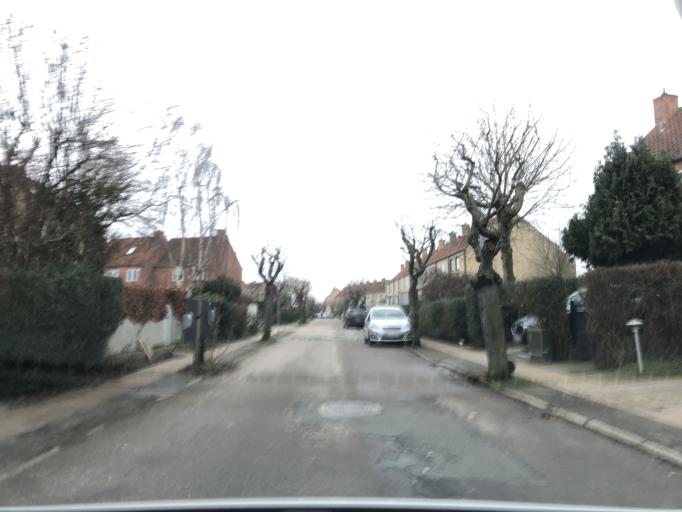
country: DK
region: Capital Region
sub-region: Tarnby Kommune
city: Tarnby
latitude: 55.6219
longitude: 12.6131
